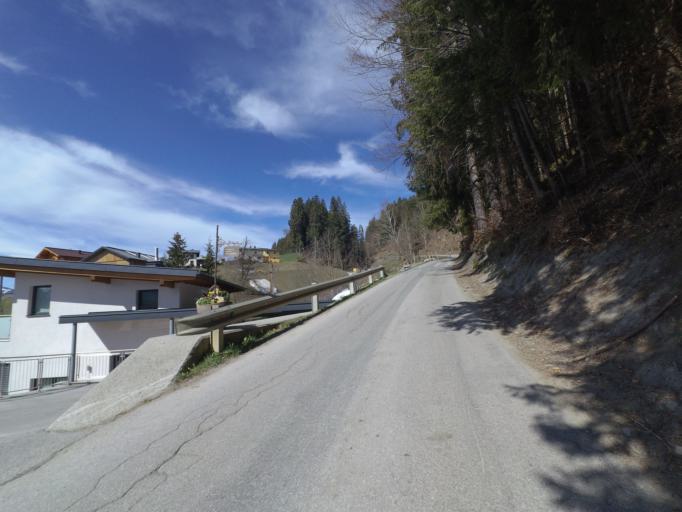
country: AT
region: Salzburg
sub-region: Politischer Bezirk Sankt Johann im Pongau
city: Sankt Veit im Pongau
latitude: 47.3344
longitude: 13.1436
